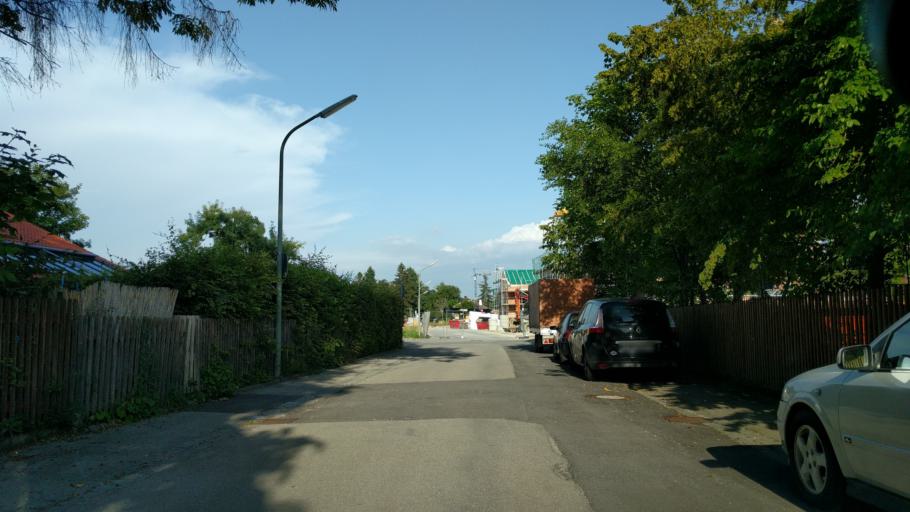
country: DE
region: Bavaria
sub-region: Upper Bavaria
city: Grunwald
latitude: 48.0396
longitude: 11.5276
